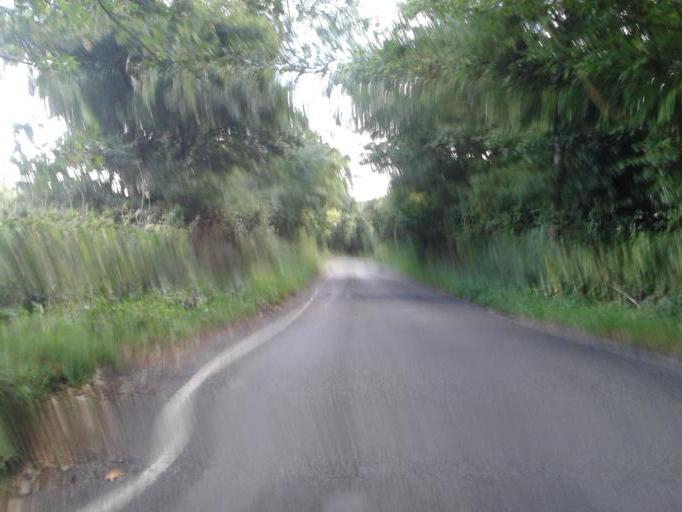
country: GB
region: England
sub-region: Cambridgeshire
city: Duxford
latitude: 52.0116
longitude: 0.1244
